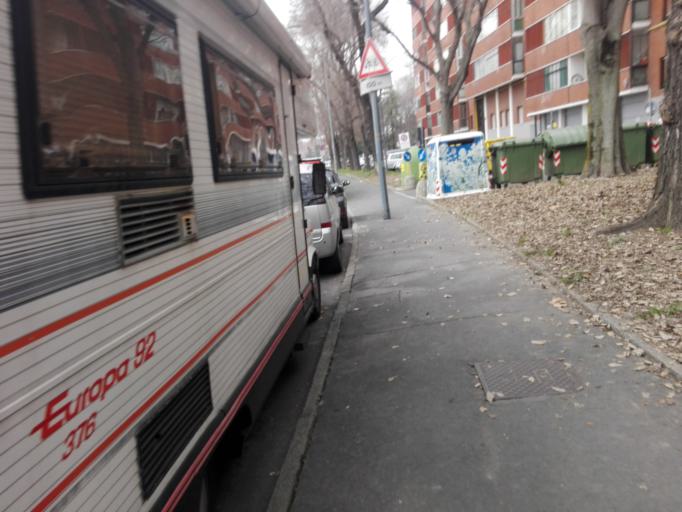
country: IT
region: Lombardy
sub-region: Citta metropolitana di Milano
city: Assago
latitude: 45.4302
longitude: 9.1604
